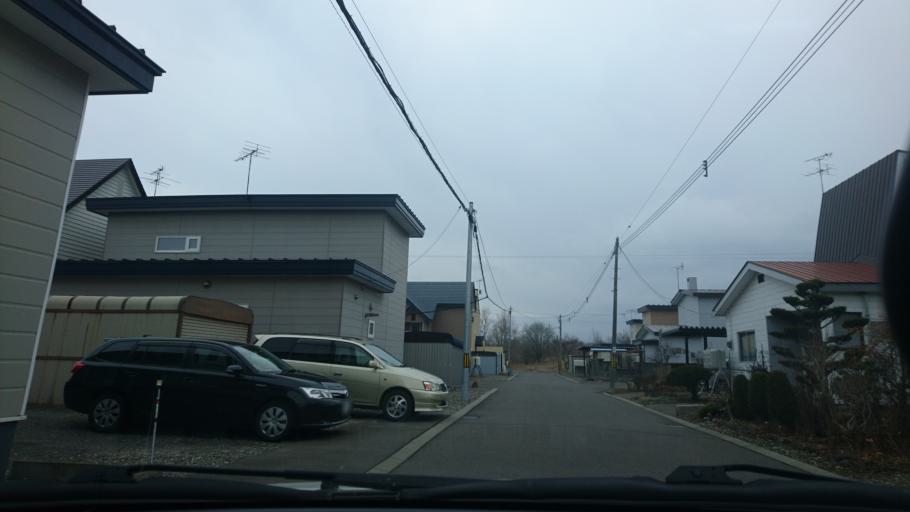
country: JP
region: Hokkaido
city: Otofuke
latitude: 42.9915
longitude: 143.2064
